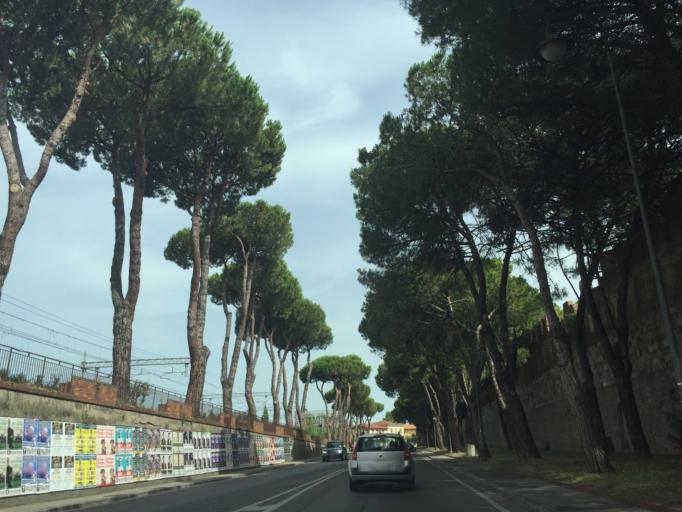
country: IT
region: Tuscany
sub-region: Province of Pisa
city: Pisa
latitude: 43.7138
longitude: 10.3886
